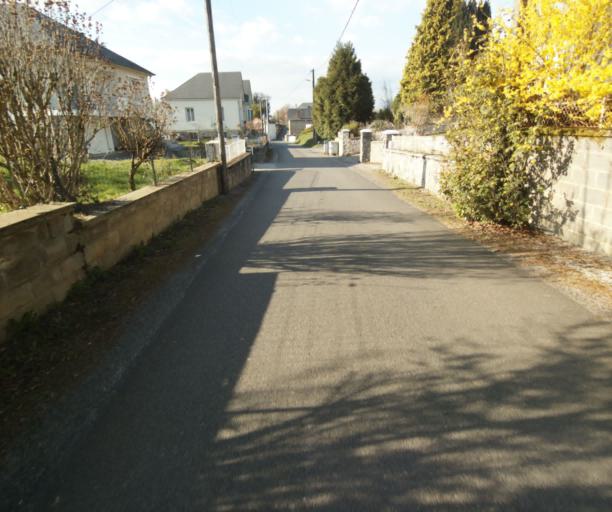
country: FR
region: Limousin
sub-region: Departement de la Correze
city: Saint-Clement
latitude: 45.3506
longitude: 1.6365
